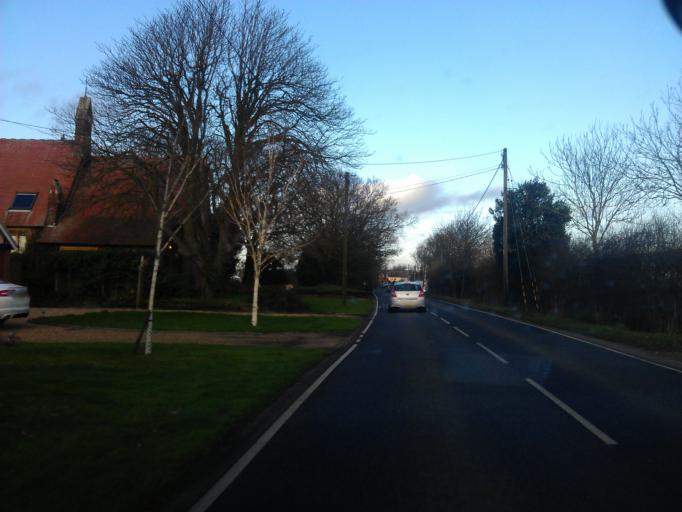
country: GB
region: England
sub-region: Essex
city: Alresford
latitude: 51.8783
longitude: 0.9939
